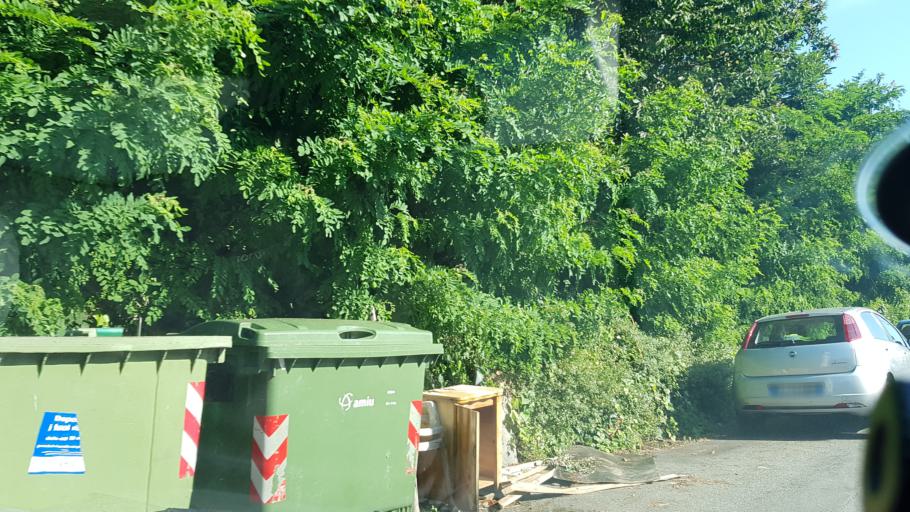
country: IT
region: Liguria
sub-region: Provincia di Genova
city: Genoa
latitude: 44.4431
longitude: 8.8966
